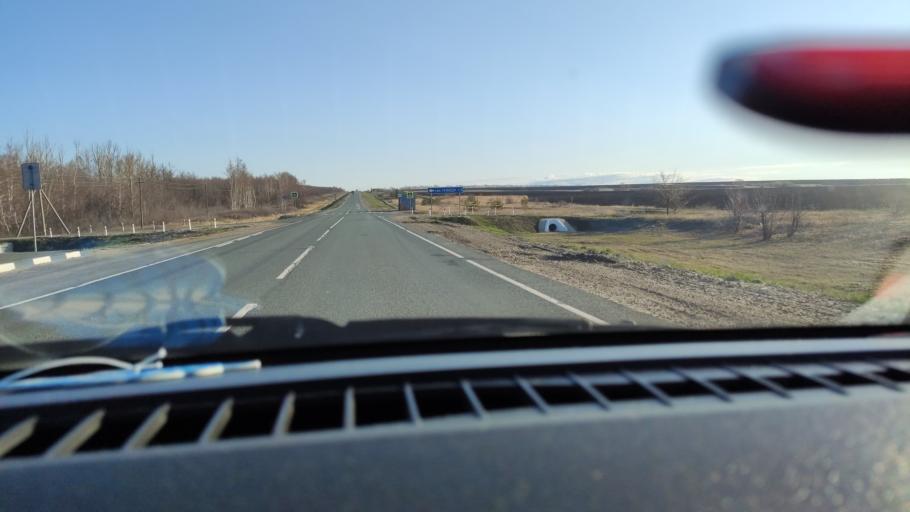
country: RU
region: Saratov
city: Alekseyevka
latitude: 52.2494
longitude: 47.9112
